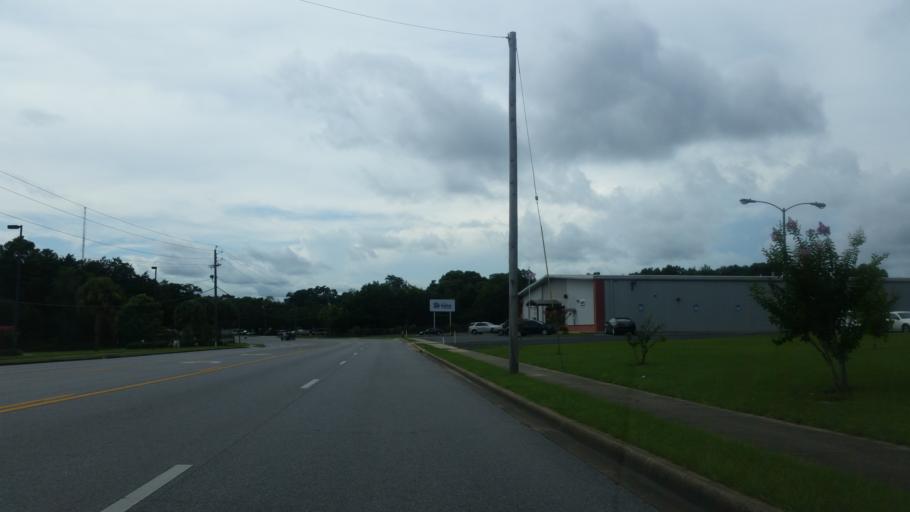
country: US
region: Florida
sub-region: Escambia County
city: Goulding
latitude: 30.4401
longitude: -87.2263
